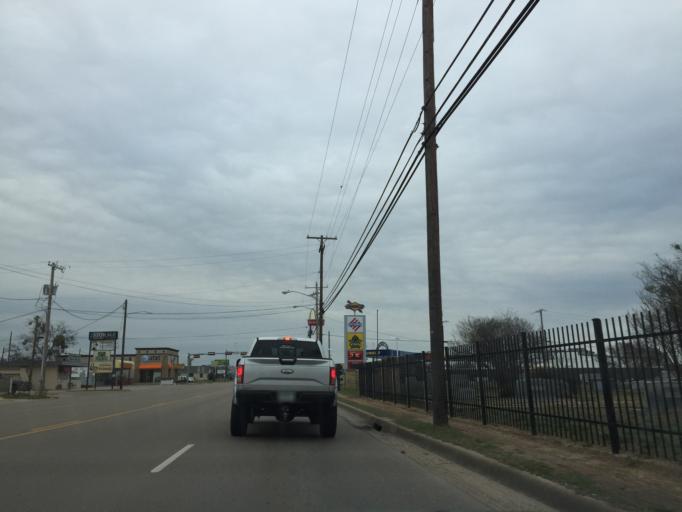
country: US
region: Texas
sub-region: Coryell County
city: Gatesville
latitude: 31.4348
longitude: -97.7338
